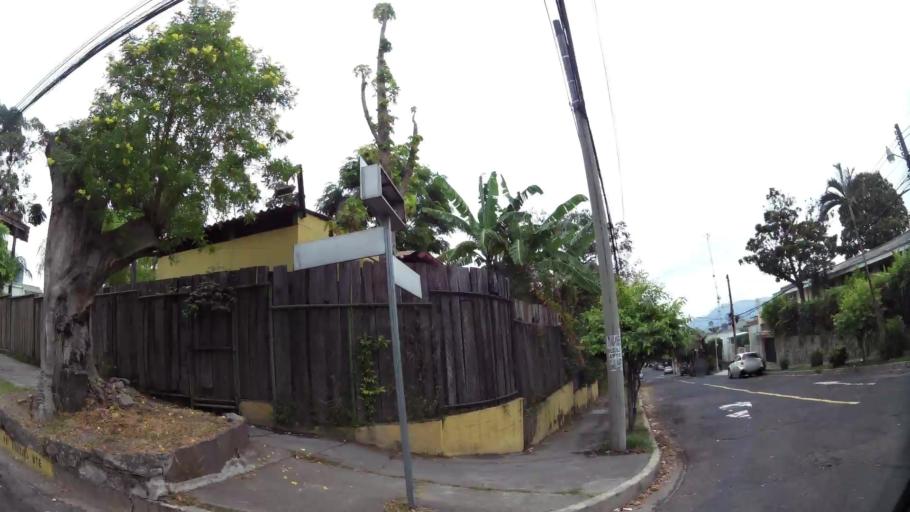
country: SV
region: La Libertad
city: Antiguo Cuscatlan
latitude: 13.7040
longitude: -89.2420
